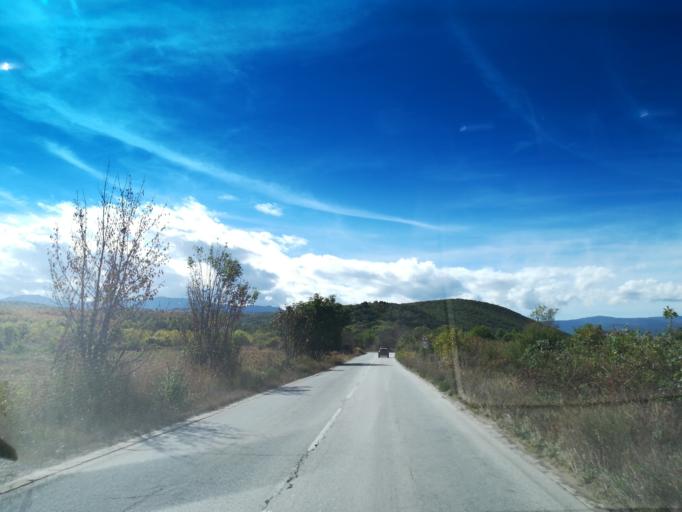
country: BG
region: Pazardzhik
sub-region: Obshtina Bratsigovo
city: Bratsigovo
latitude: 42.0711
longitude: 24.4039
